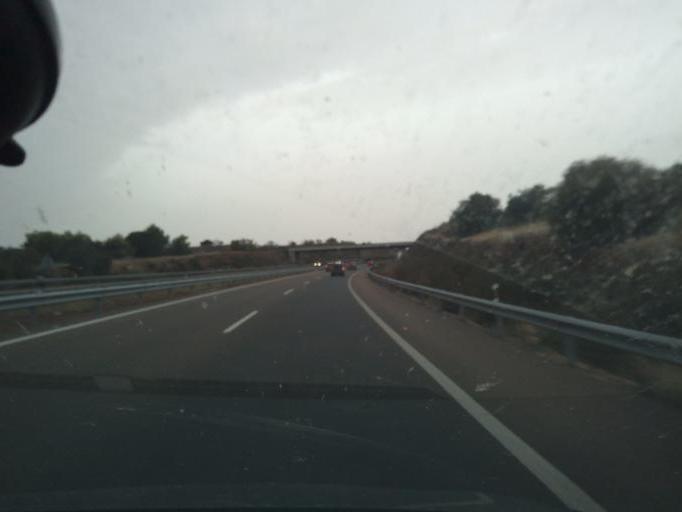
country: ES
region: Extremadura
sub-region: Provincia de Badajoz
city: San Pedro de Merida
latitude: 38.9455
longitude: -6.1837
